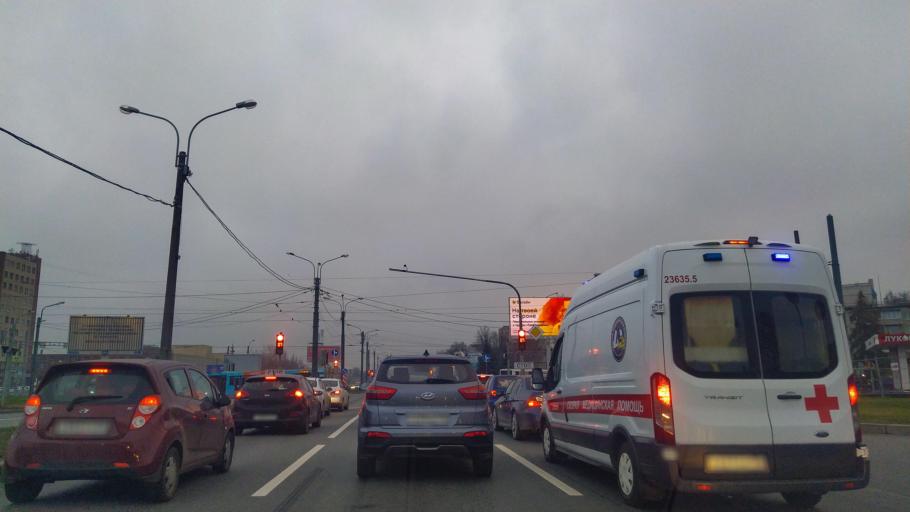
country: RU
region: Leningrad
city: Akademicheskoe
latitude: 60.0048
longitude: 30.4357
